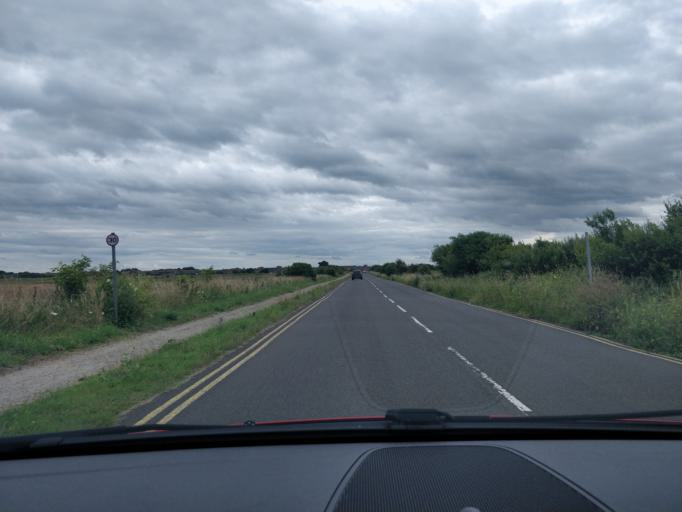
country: GB
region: England
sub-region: Sefton
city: Southport
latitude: 53.6754
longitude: -2.9802
